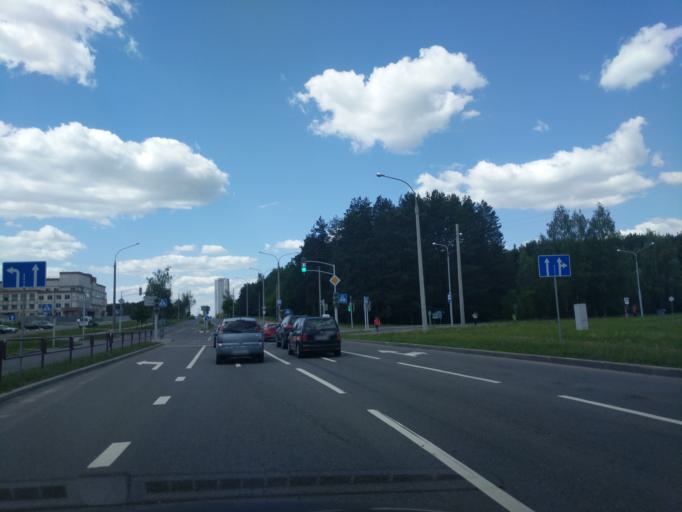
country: BY
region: Minsk
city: Borovlyany
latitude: 53.9248
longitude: 27.6672
